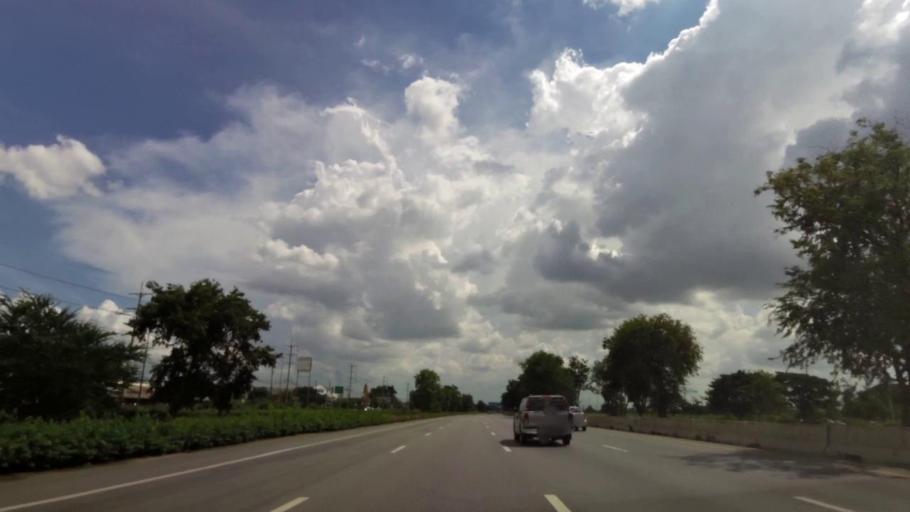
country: TH
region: Phra Nakhon Si Ayutthaya
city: Phra Nakhon Si Ayutthaya
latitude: 14.3721
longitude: 100.6101
